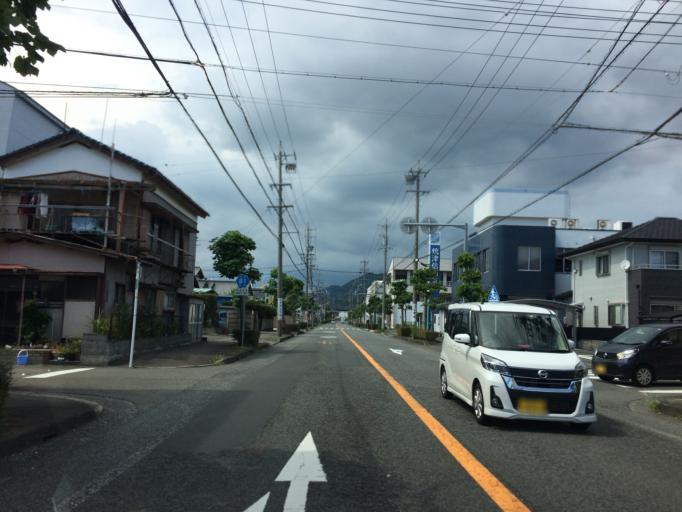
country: JP
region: Shizuoka
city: Yaizu
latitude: 34.8730
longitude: 138.3134
